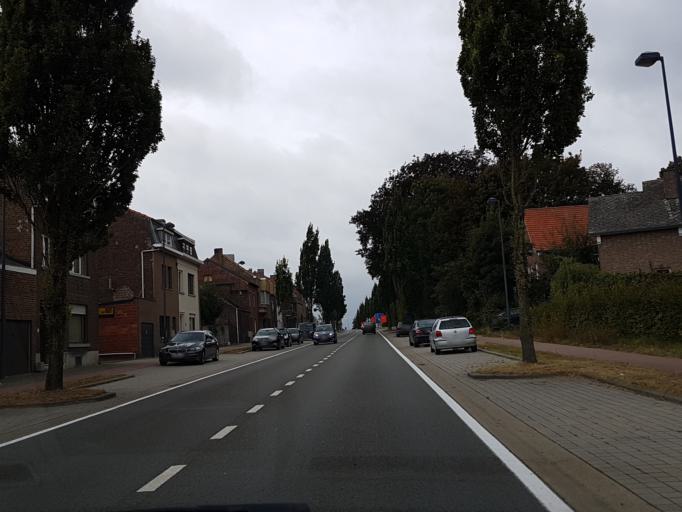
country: BE
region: Flanders
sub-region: Provincie Vlaams-Brabant
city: Tienen
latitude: 50.7988
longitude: 4.9770
